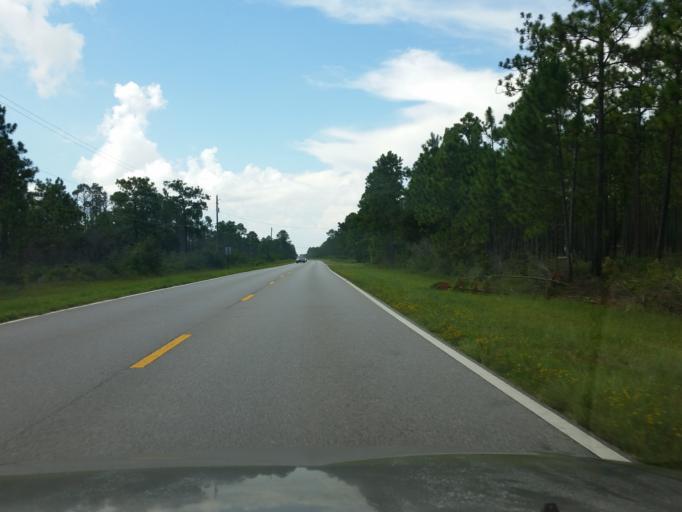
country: US
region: Florida
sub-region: Escambia County
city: Myrtle Grove
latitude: 30.3741
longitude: -87.4023
